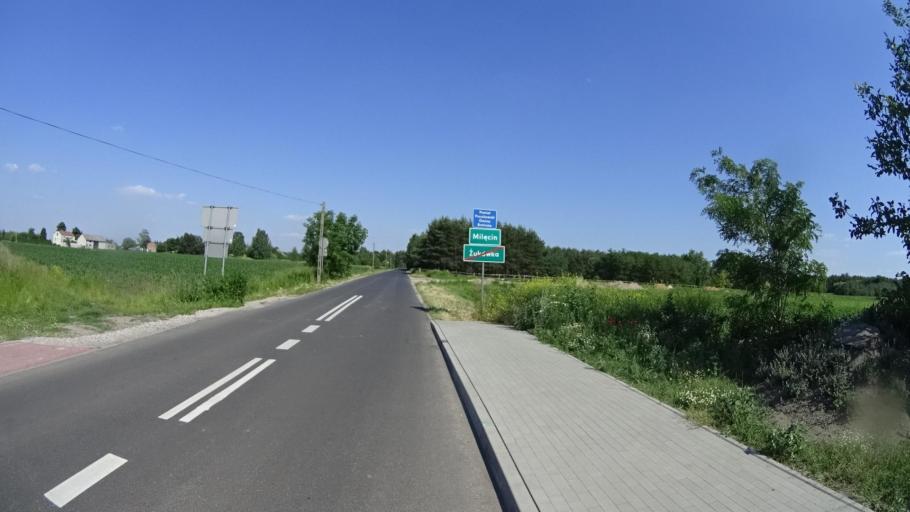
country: PL
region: Masovian Voivodeship
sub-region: Powiat warszawski zachodni
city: Blonie
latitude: 52.1653
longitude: 20.6307
